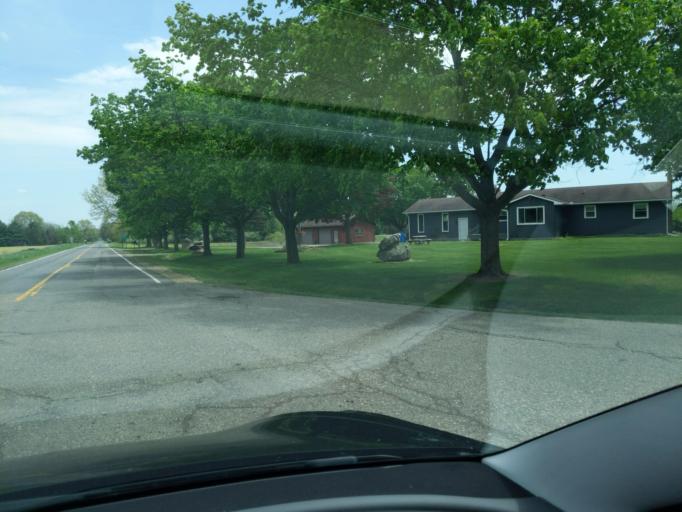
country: US
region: Michigan
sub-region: Ingham County
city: Stockbridge
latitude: 42.4832
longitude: -84.2583
